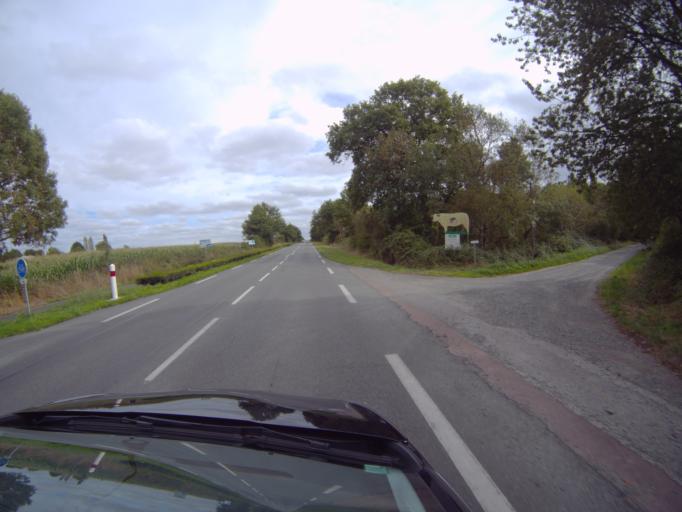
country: FR
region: Pays de la Loire
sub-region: Departement de la Vendee
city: Saint-Hilaire-de-Loulay
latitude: 46.9927
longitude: -1.3253
